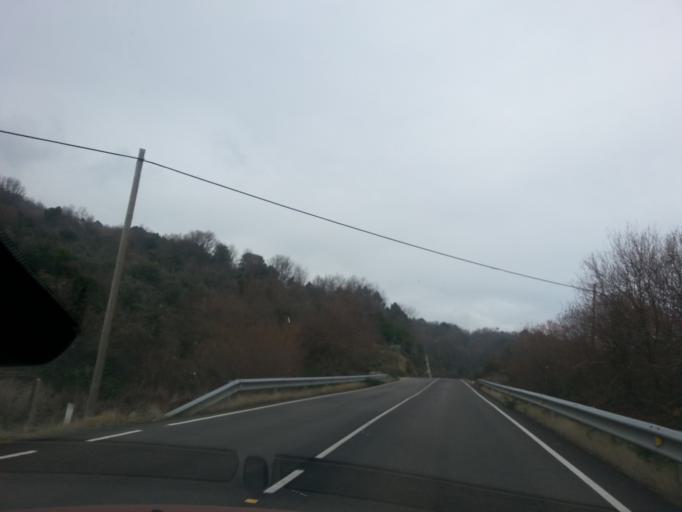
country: ES
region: Castille and Leon
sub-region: Provincia de Salamanca
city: Herguijuela de la Sierra
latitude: 40.4535
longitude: -6.0668
